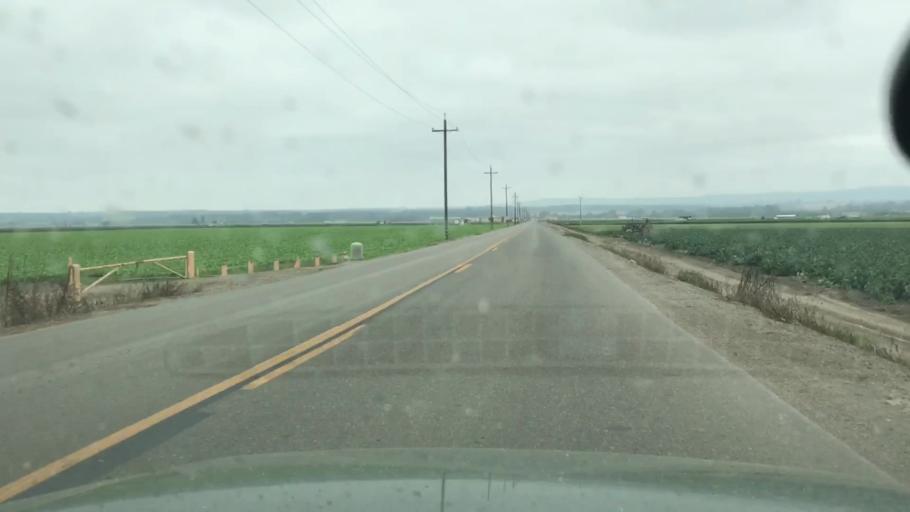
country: US
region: California
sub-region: Santa Barbara County
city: Lompoc
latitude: 34.6405
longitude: -120.4933
